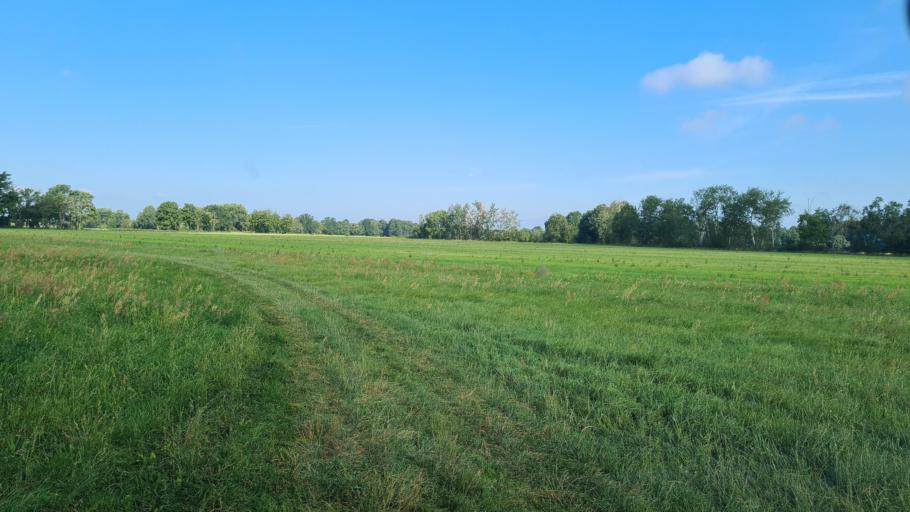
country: DE
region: Brandenburg
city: Finsterwalde
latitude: 51.6567
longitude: 13.7287
